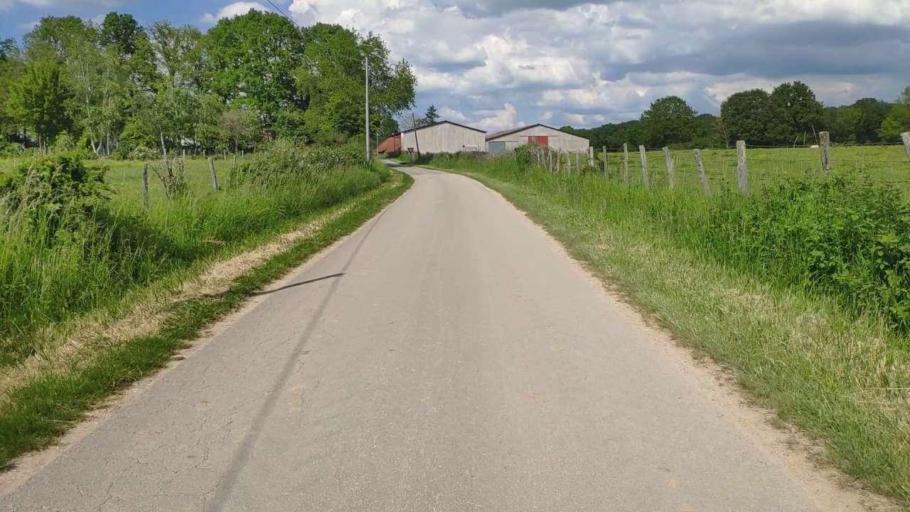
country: FR
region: Franche-Comte
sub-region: Departement du Jura
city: Bletterans
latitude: 46.8278
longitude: 5.4073
